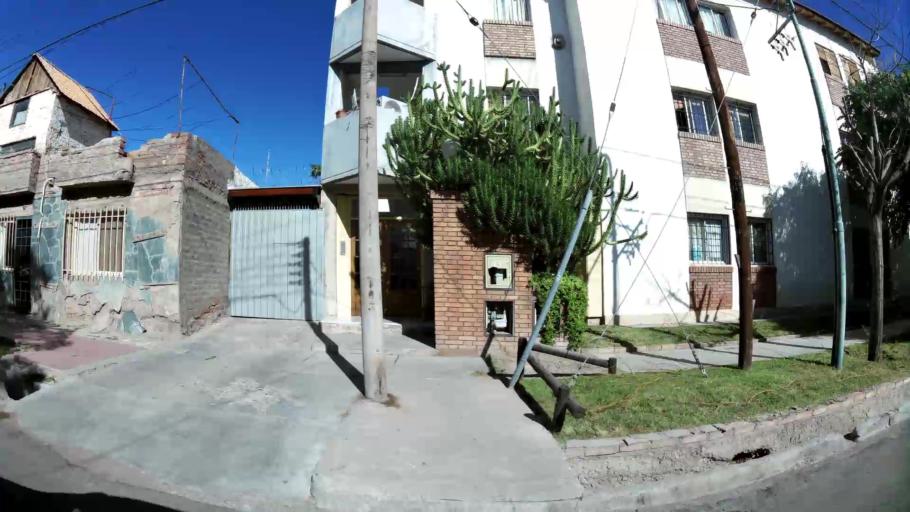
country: AR
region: Mendoza
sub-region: Departamento de Godoy Cruz
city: Godoy Cruz
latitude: -32.9331
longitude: -68.8610
